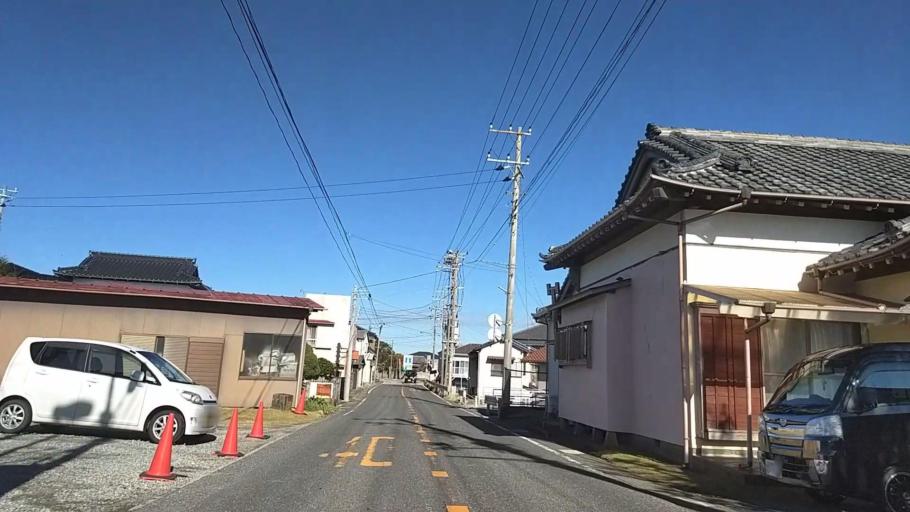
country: JP
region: Chiba
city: Tateyama
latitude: 34.9473
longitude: 139.9629
